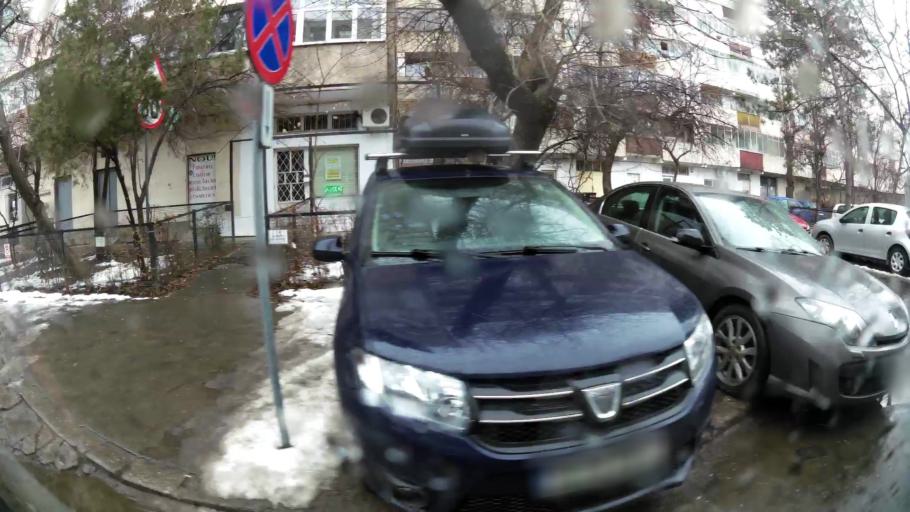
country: RO
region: Ilfov
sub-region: Comuna Chiajna
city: Rosu
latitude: 44.4143
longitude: 26.0239
